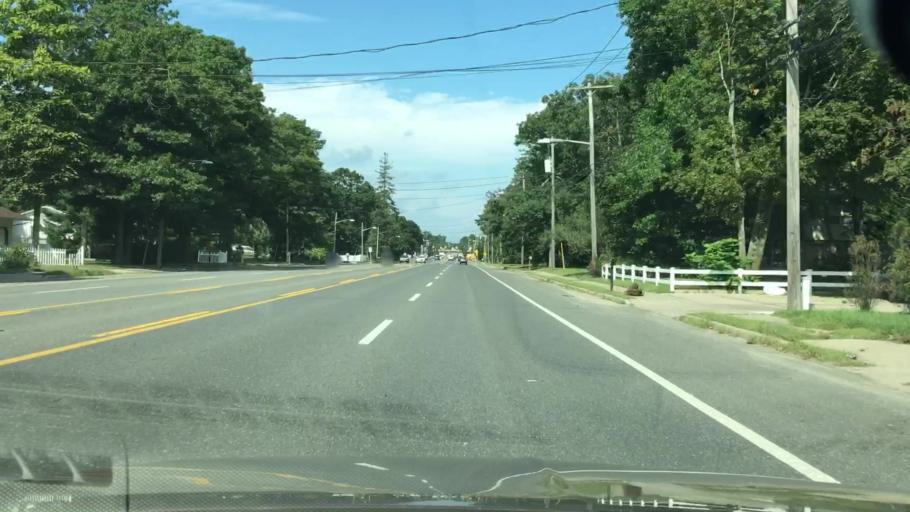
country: US
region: New York
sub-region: Suffolk County
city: Ronkonkoma
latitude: 40.8028
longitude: -73.1235
